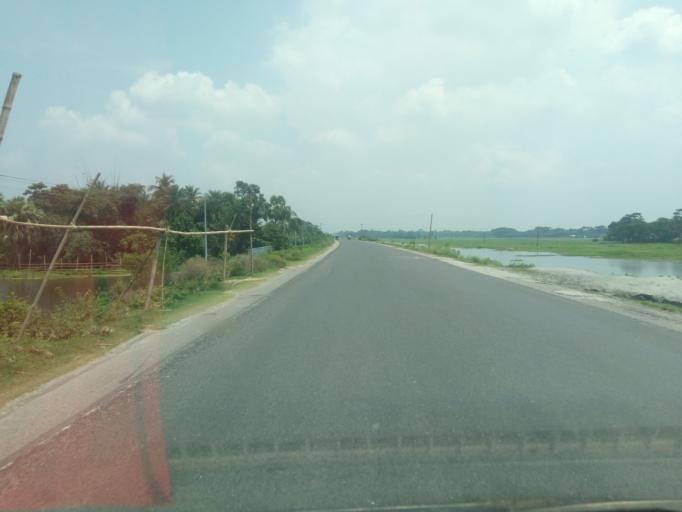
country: BD
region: Dhaka
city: Char Bhadrasan
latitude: 23.3799
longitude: 90.0077
